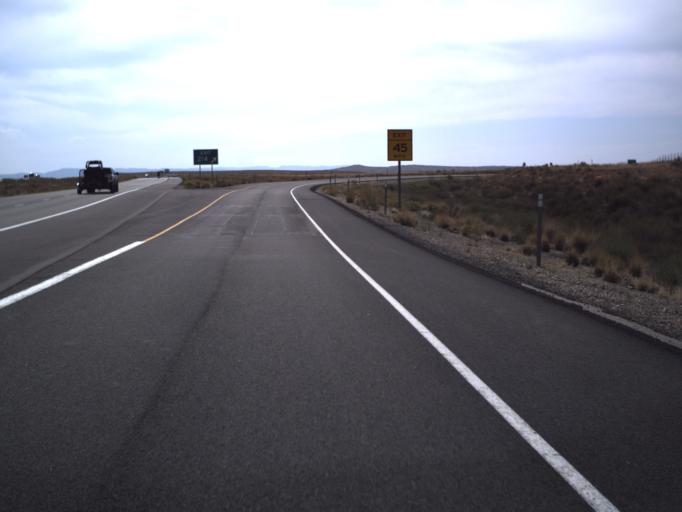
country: US
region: Colorado
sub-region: Mesa County
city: Loma
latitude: 39.0414
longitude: -109.2789
